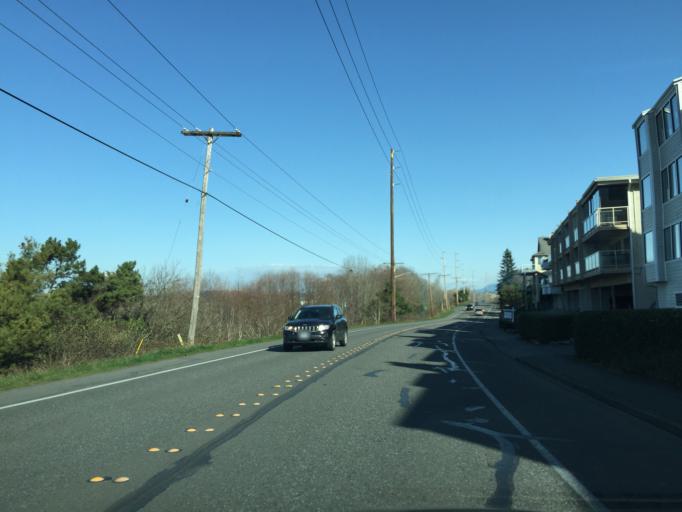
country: US
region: Washington
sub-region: Whatcom County
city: Bellingham
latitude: 48.7399
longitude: -122.4913
